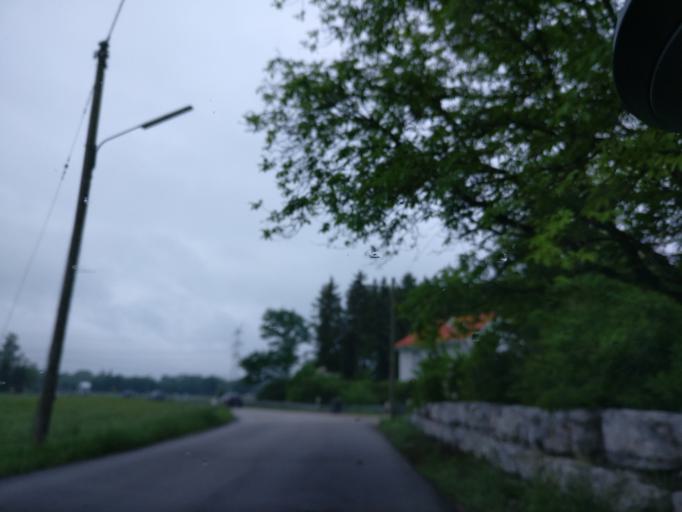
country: DE
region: Bavaria
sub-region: Upper Bavaria
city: Dachau
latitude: 48.2233
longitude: 11.4224
